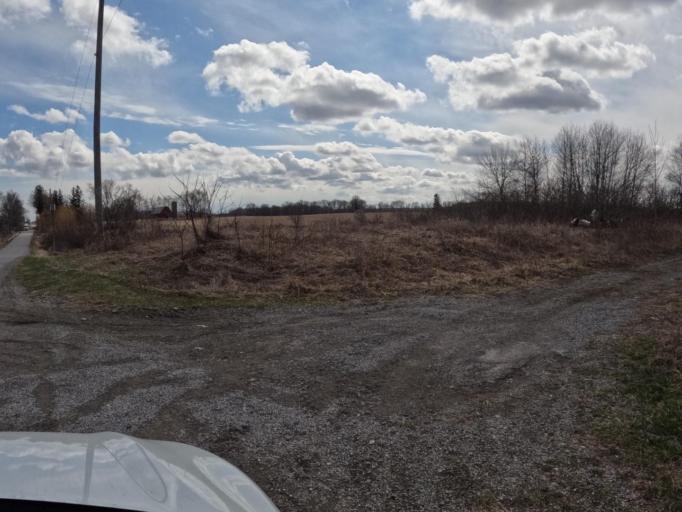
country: CA
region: Ontario
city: Norfolk County
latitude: 42.9355
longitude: -80.2033
